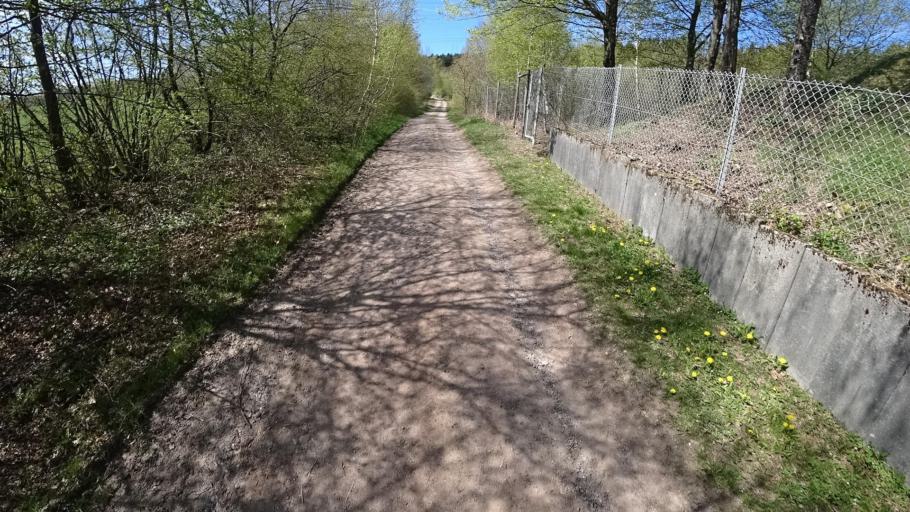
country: DE
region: Rheinland-Pfalz
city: Gusenburg
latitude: 49.6326
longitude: 6.8933
